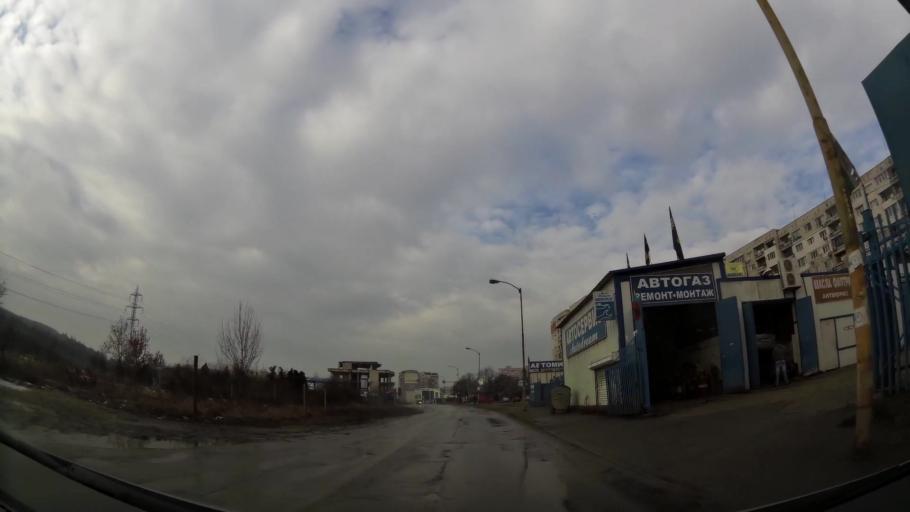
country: BG
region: Sofia-Capital
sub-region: Stolichna Obshtina
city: Sofia
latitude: 42.7096
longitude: 23.2613
